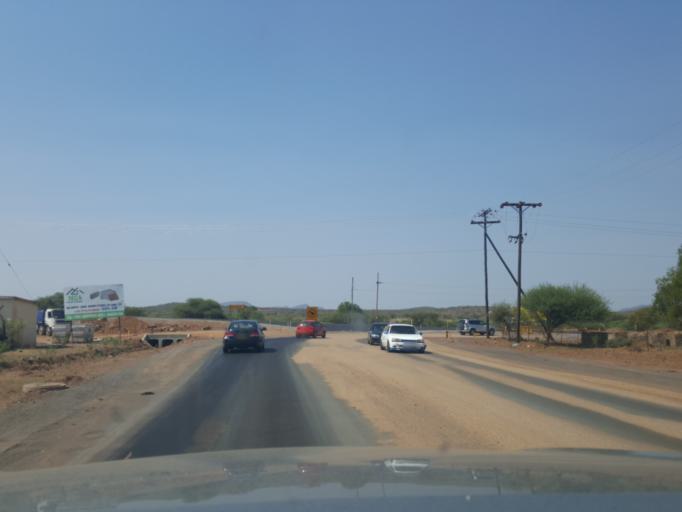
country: BW
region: South East
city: Ramotswa
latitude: -24.8304
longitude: 25.8094
